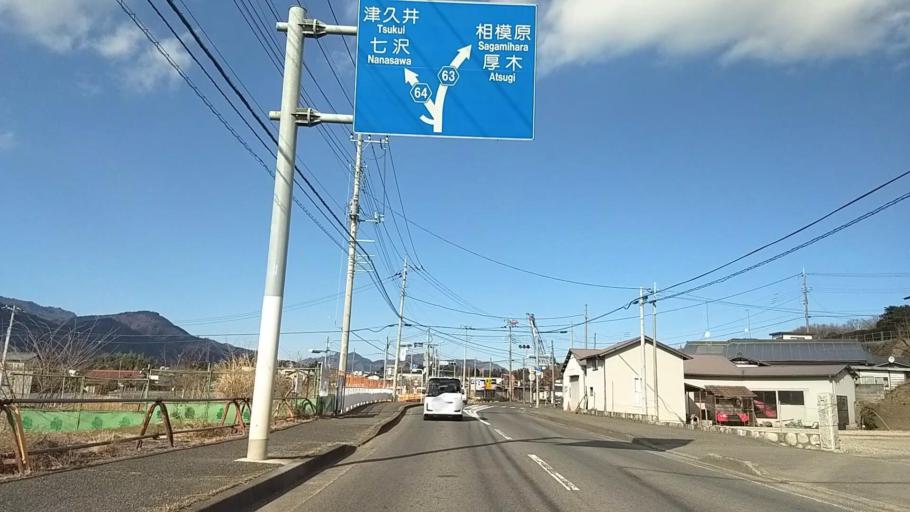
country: JP
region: Kanagawa
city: Isehara
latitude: 35.4227
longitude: 139.3022
